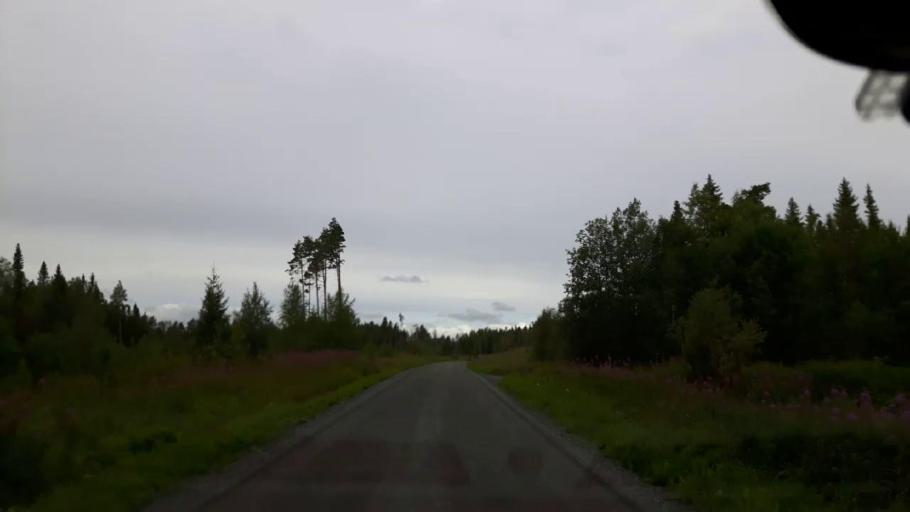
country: SE
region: Jaemtland
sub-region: Krokoms Kommun
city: Krokom
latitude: 63.2772
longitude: 14.3962
